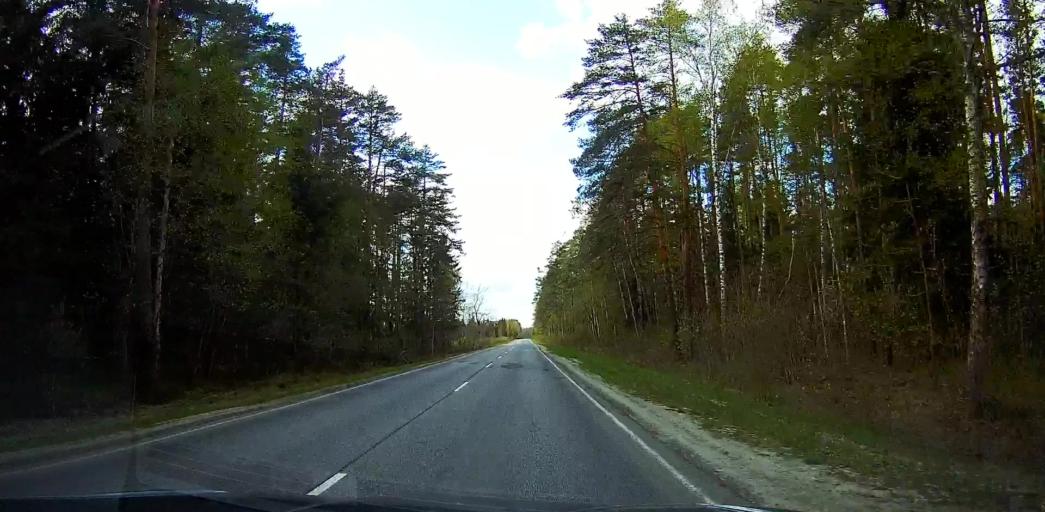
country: RU
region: Moskovskaya
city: Rakhmanovo
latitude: 55.6472
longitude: 38.6717
